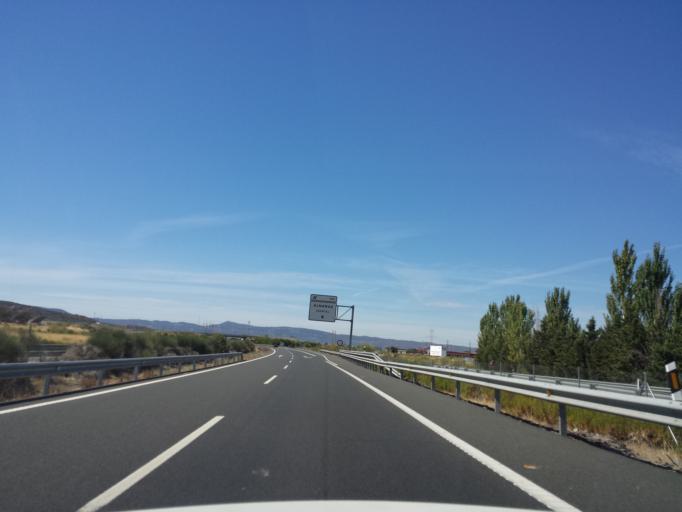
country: ES
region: Extremadura
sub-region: Provincia de Caceres
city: Almaraz
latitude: 39.8320
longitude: -5.6549
